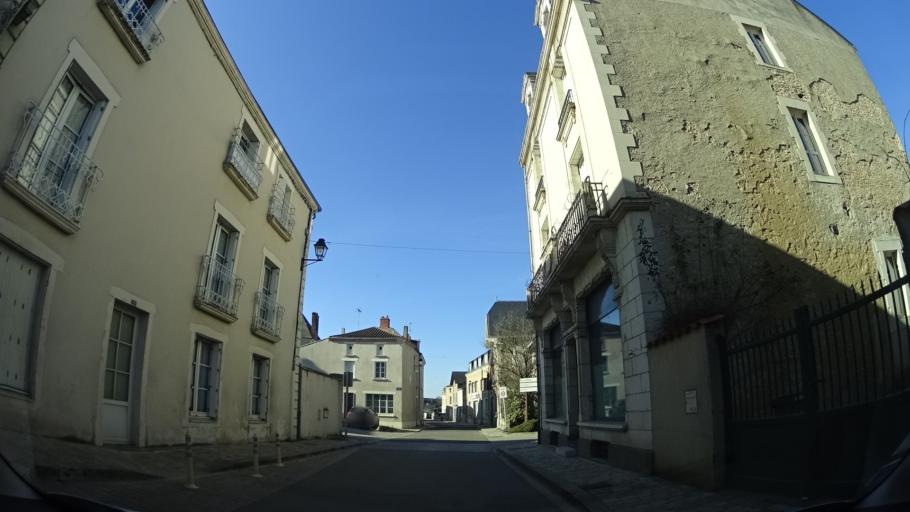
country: FR
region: Poitou-Charentes
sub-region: Departement des Deux-Sevres
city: Airvault
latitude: 46.8262
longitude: -0.1395
